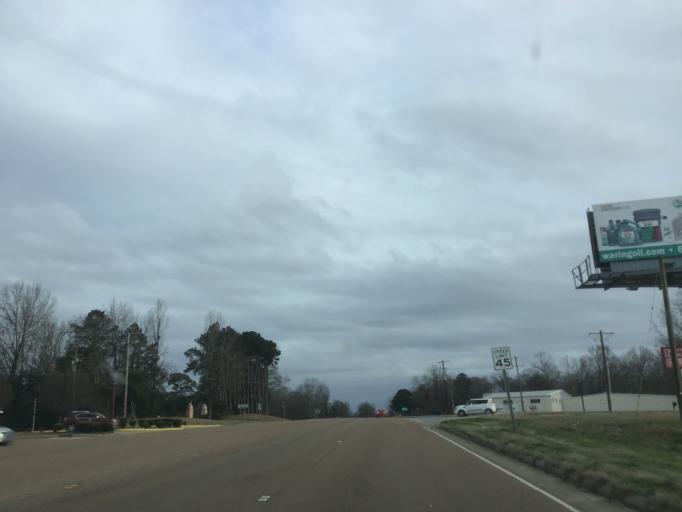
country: US
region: Mississippi
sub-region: Warren County
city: Beechwood
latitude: 32.3432
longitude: -90.8287
